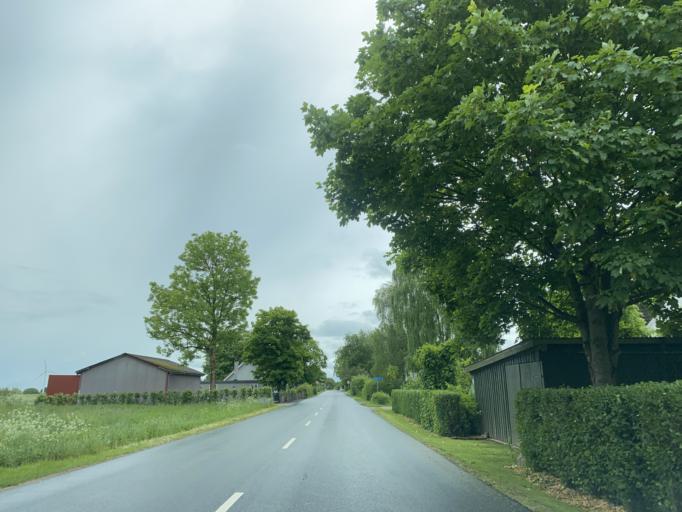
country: DK
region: Central Jutland
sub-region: Arhus Kommune
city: Sabro
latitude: 56.2561
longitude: 9.9605
